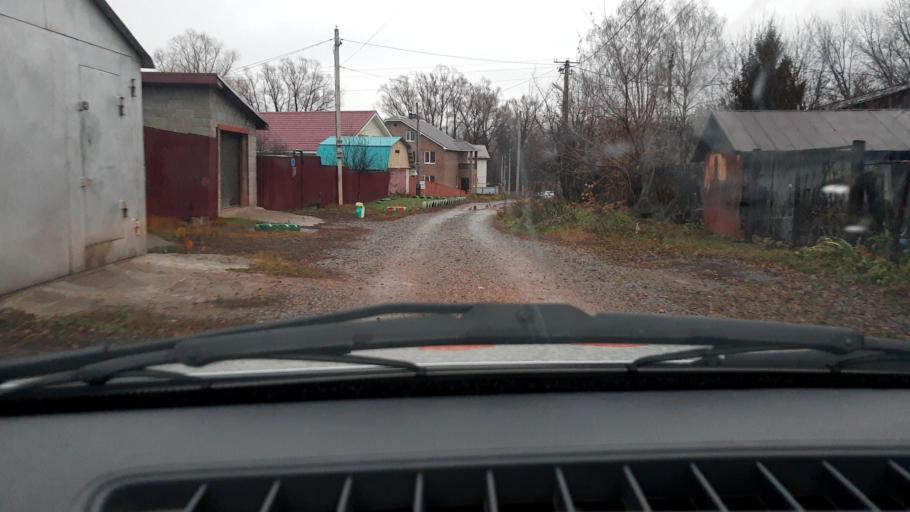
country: RU
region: Bashkortostan
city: Mikhaylovka
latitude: 54.7947
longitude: 55.8884
